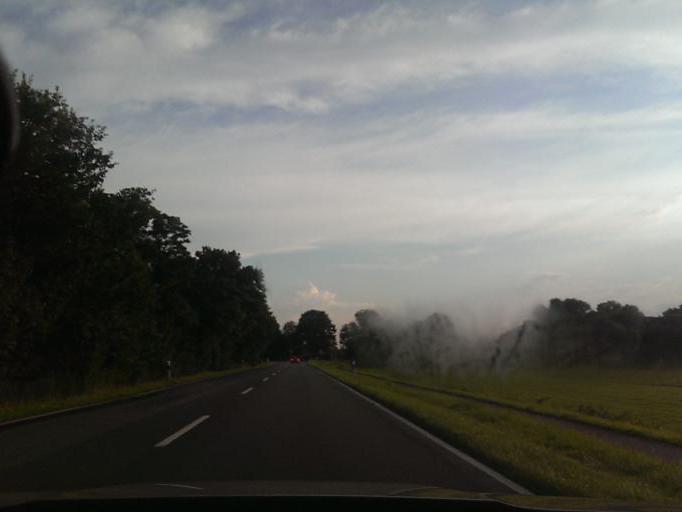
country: DE
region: Lower Saxony
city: Osterholz-Scharmbeck
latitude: 53.1866
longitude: 8.8180
